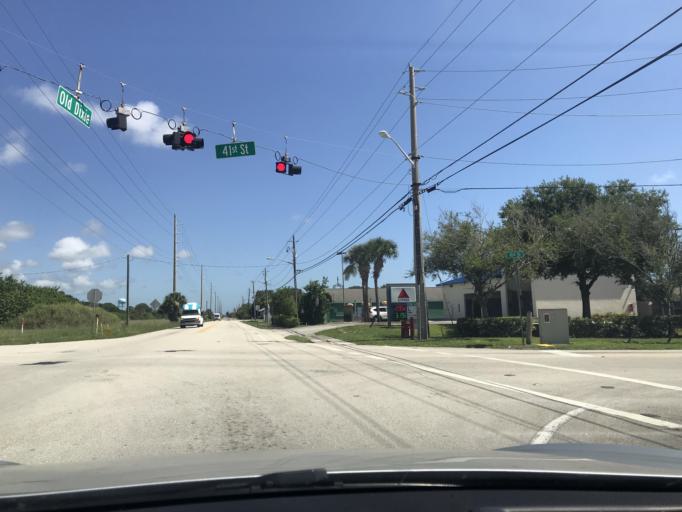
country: US
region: Florida
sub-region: Indian River County
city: Gifford
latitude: 27.6675
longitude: -80.4069
